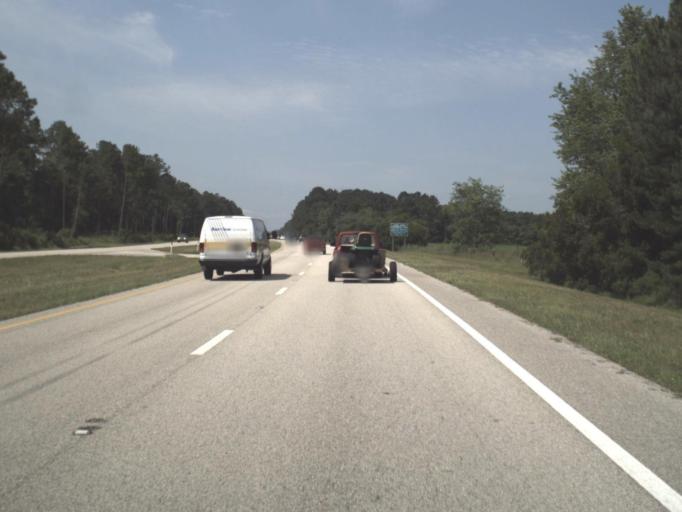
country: US
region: Florida
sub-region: Alachua County
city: Gainesville
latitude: 29.7159
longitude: -82.2683
